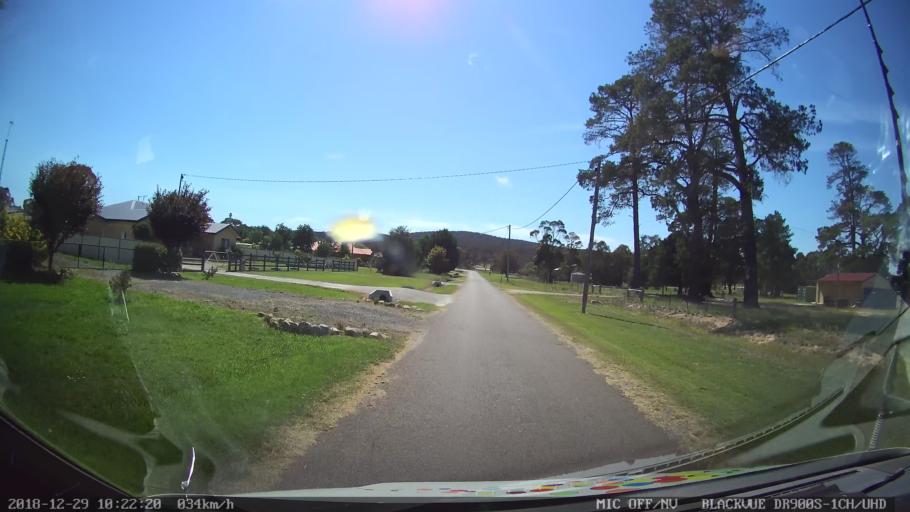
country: AU
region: New South Wales
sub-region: Yass Valley
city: Gundaroo
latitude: -34.9164
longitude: 149.4347
